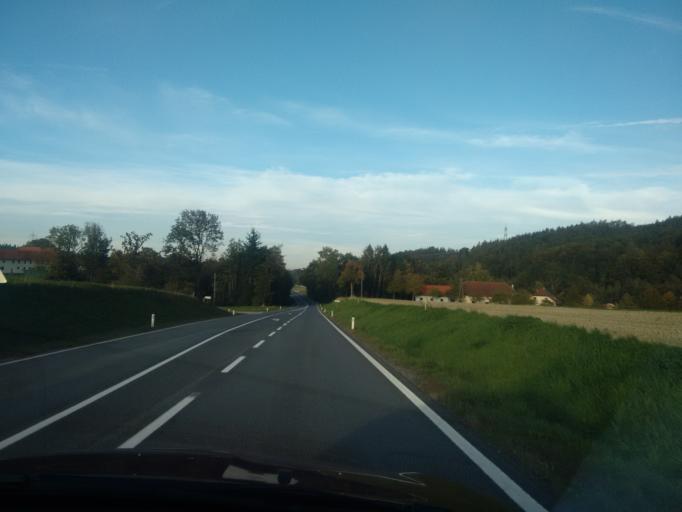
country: AT
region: Upper Austria
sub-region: Politischer Bezirk Vocklabruck
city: Niederthalheim
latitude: 48.1579
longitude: 13.7414
